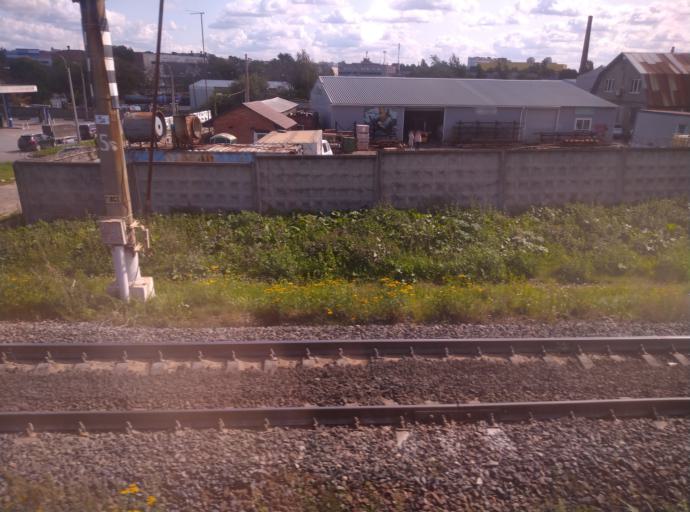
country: RU
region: St.-Petersburg
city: Centralniy
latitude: 59.9045
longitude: 30.3812
